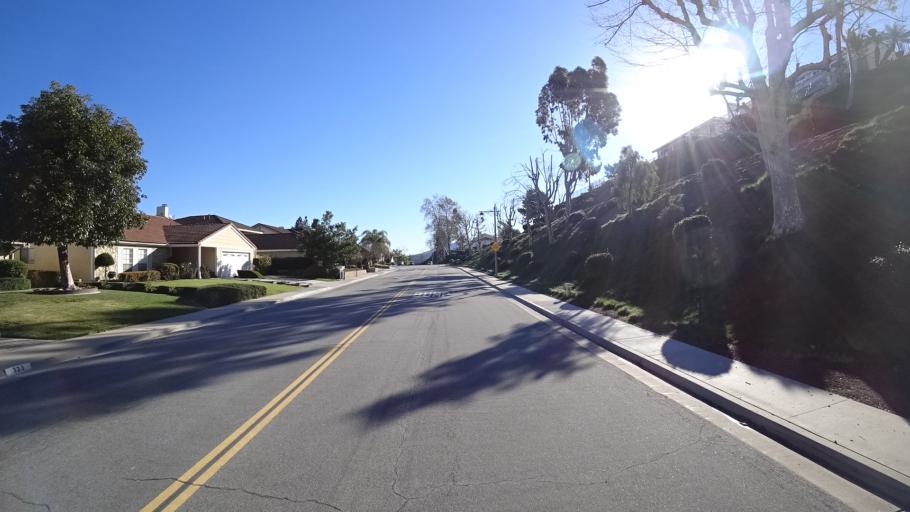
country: US
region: California
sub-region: Orange County
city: Villa Park
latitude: 33.8485
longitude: -117.7991
